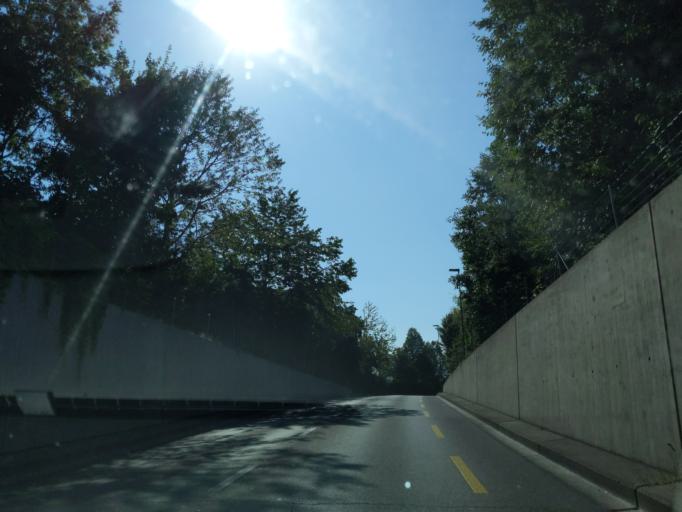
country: CH
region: Bern
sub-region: Thun District
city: Thun
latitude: 46.7248
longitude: 7.6206
